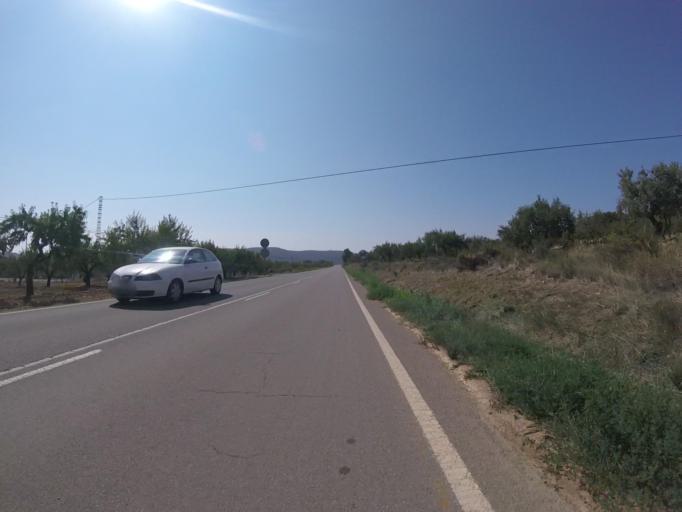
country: ES
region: Valencia
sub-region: Provincia de Castello
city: Adzaneta
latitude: 40.2337
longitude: -0.1774
